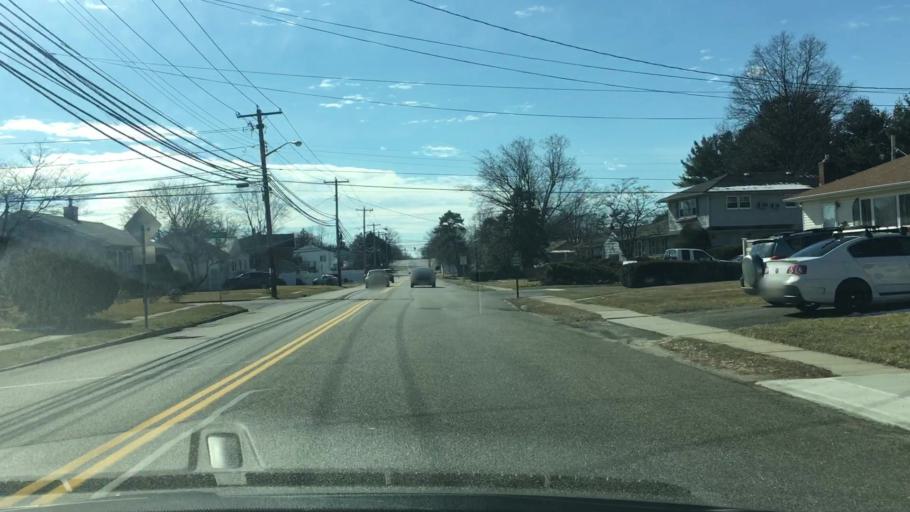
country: US
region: New York
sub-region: Suffolk County
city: West Babylon
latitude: 40.7173
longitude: -73.3477
